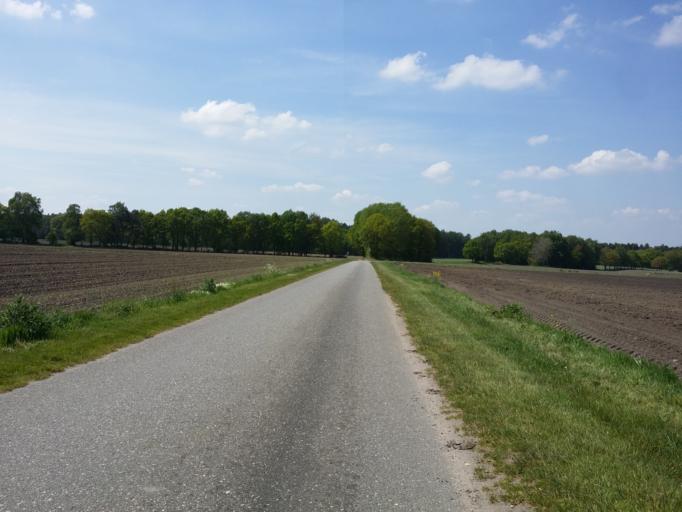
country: DE
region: Lower Saxony
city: Wulsbuttel
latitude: 53.2910
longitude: 8.6616
